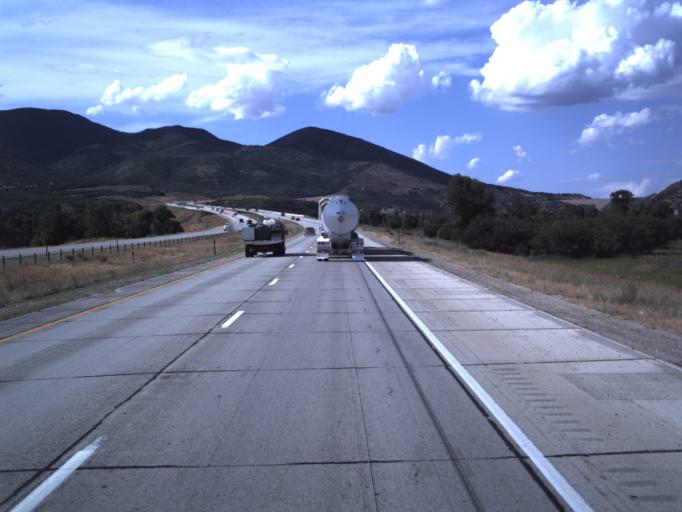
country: US
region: Utah
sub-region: Wasatch County
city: Heber
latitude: 40.5647
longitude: -111.4285
